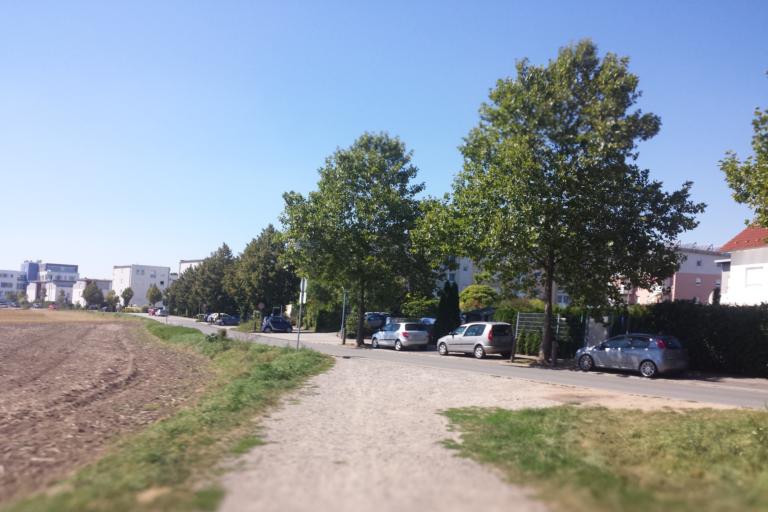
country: DE
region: Hesse
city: Viernheim
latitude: 49.5417
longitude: 8.5996
